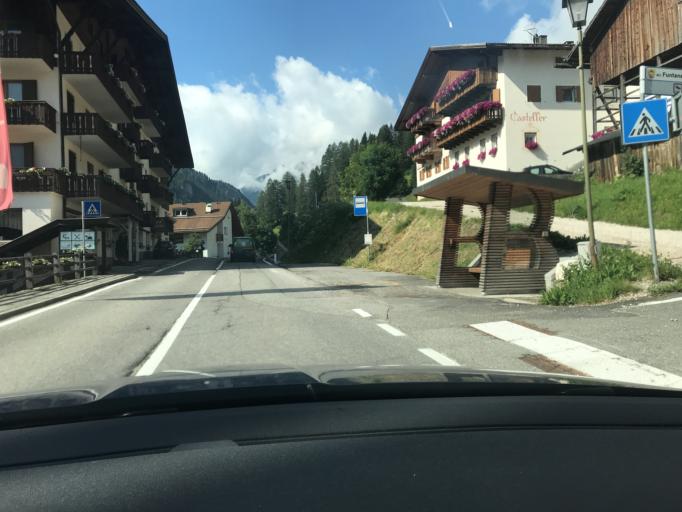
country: IT
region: Trentino-Alto Adige
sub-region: Bolzano
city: Corvara in Badia
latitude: 46.5743
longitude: 11.8928
